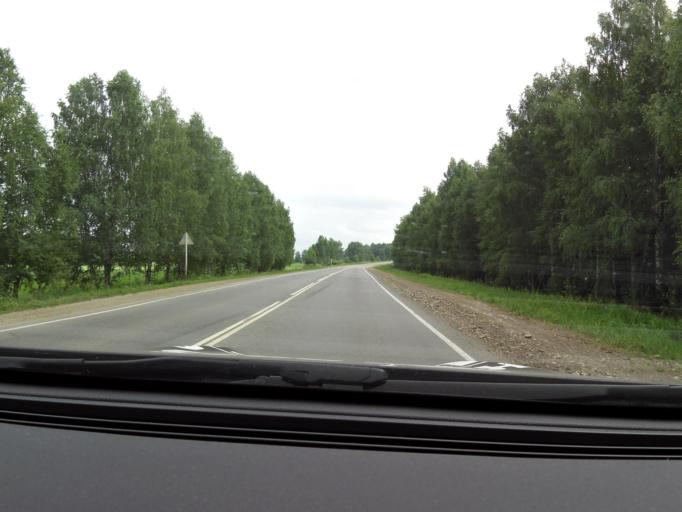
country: RU
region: Perm
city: Kukushtan
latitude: 57.4832
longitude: 56.6868
